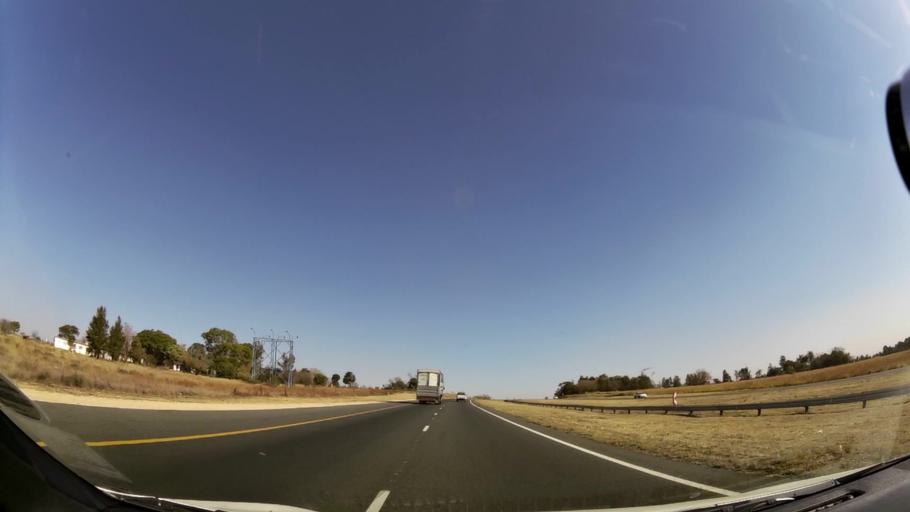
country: ZA
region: Gauteng
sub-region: City of Johannesburg Metropolitan Municipality
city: Diepsloot
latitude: -25.9678
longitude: 27.9469
